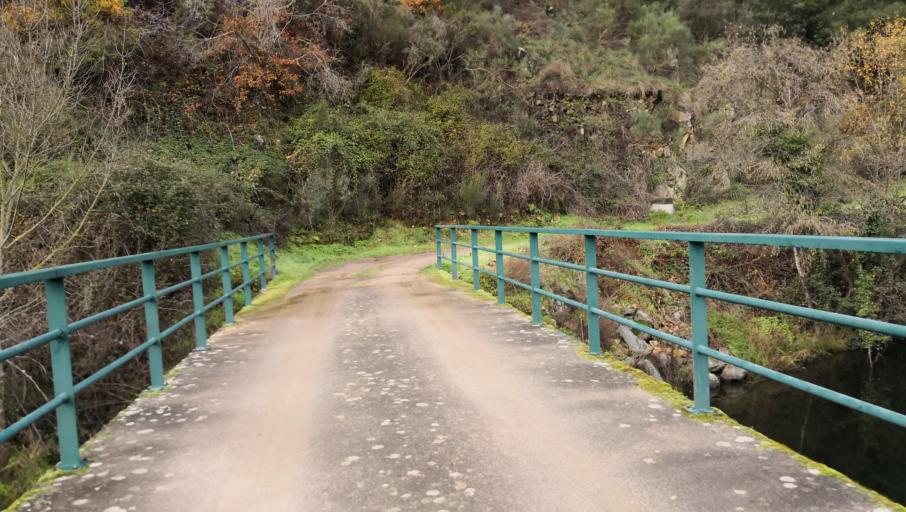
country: PT
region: Vila Real
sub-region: Vila Real
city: Vila Real
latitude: 41.2884
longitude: -7.7493
